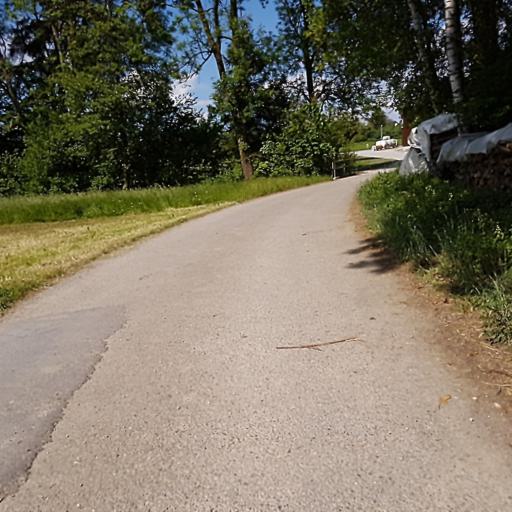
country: CH
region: Thurgau
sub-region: Arbon District
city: Amriswil
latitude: 47.5598
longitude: 9.2997
